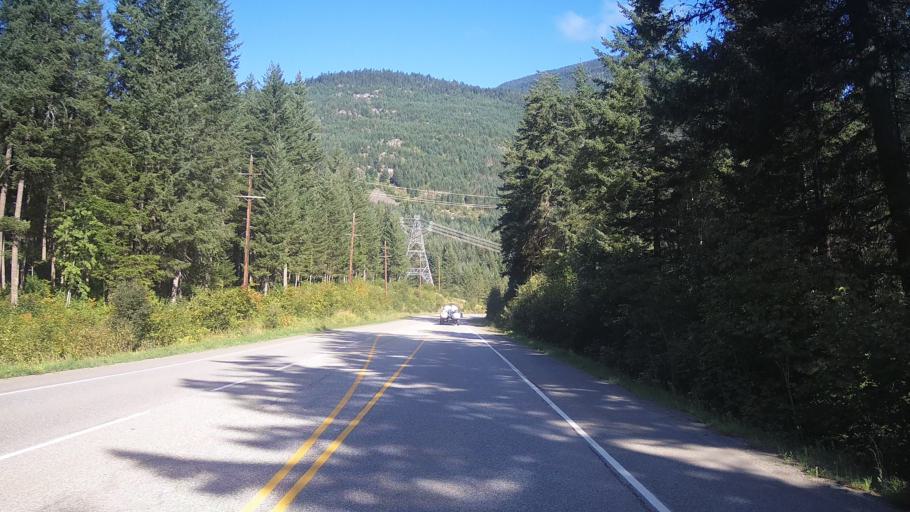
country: CA
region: British Columbia
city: Hope
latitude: 49.6621
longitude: -121.4149
